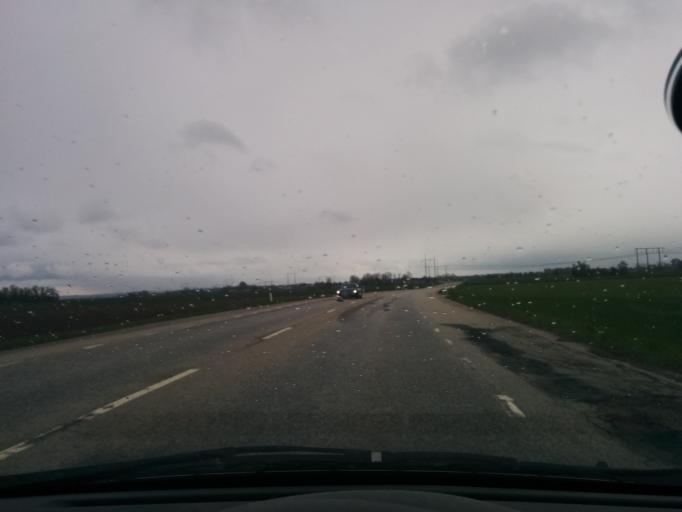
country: SE
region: Skane
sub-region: Staffanstorps Kommun
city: Hjaerup
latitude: 55.6413
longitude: 13.1572
